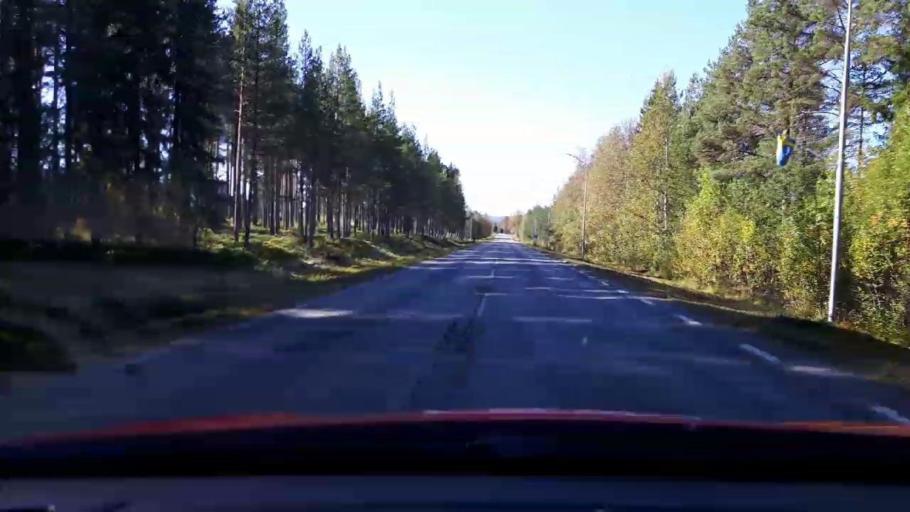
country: SE
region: Jaemtland
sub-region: Harjedalens Kommun
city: Sveg
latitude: 62.3187
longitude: 14.0550
